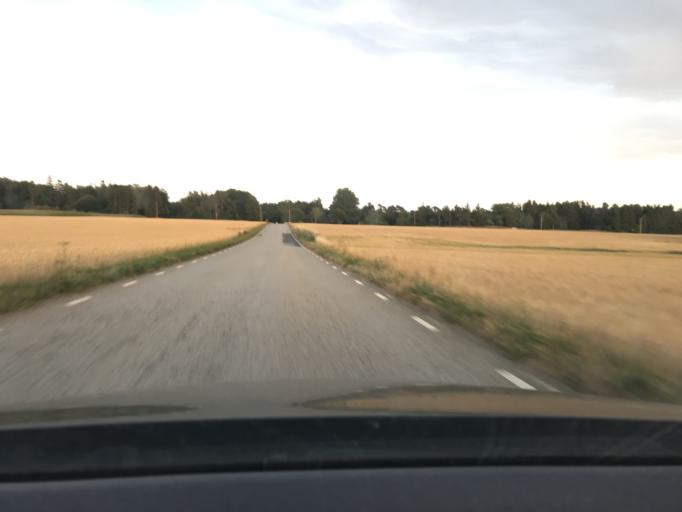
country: SE
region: Skane
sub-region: Simrishamns Kommun
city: Simrishamn
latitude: 55.4381
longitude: 14.2262
